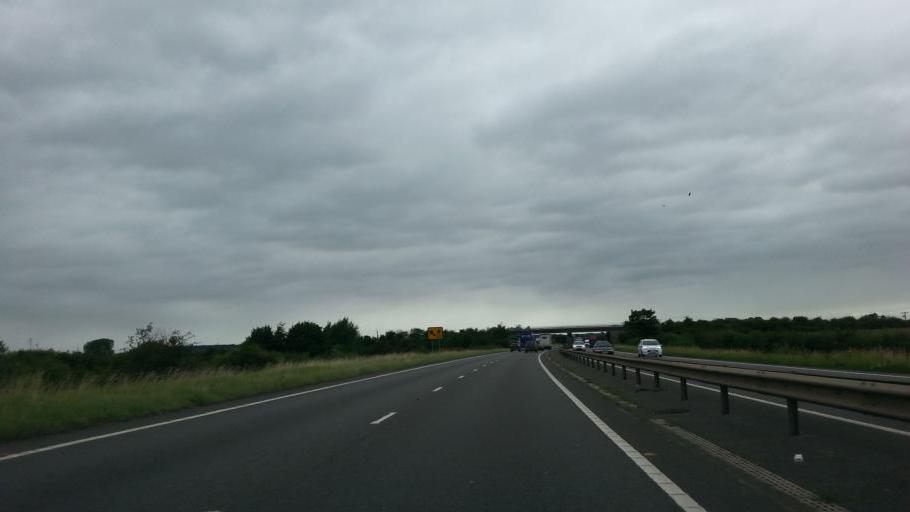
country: GB
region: England
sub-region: Nottinghamshire
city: Newark on Trent
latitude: 53.1079
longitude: -0.8106
